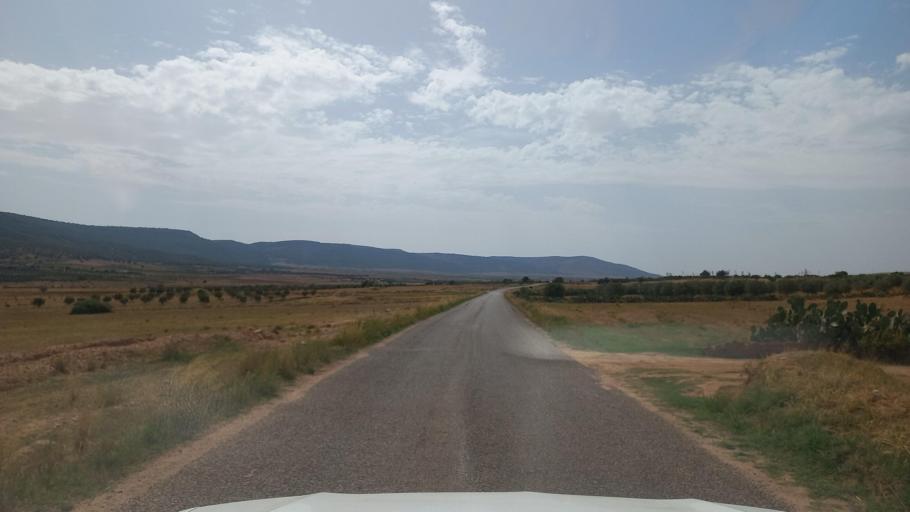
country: TN
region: Al Qasrayn
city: Kasserine
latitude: 35.3678
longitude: 8.8834
